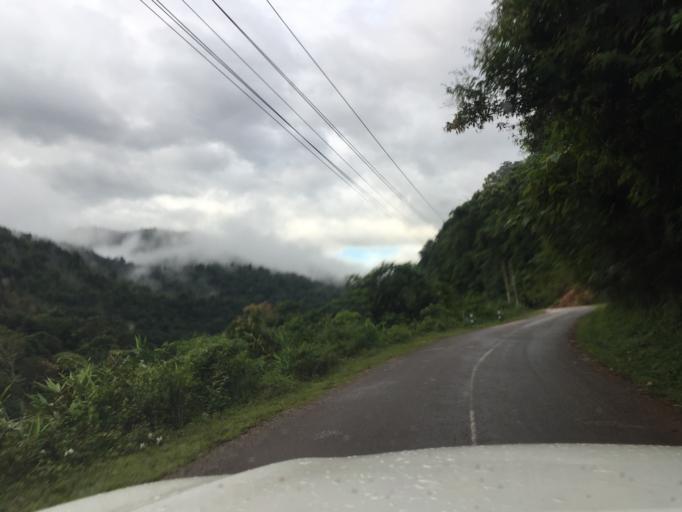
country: LA
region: Oudomxai
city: Muang La
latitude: 20.8709
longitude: 102.1327
